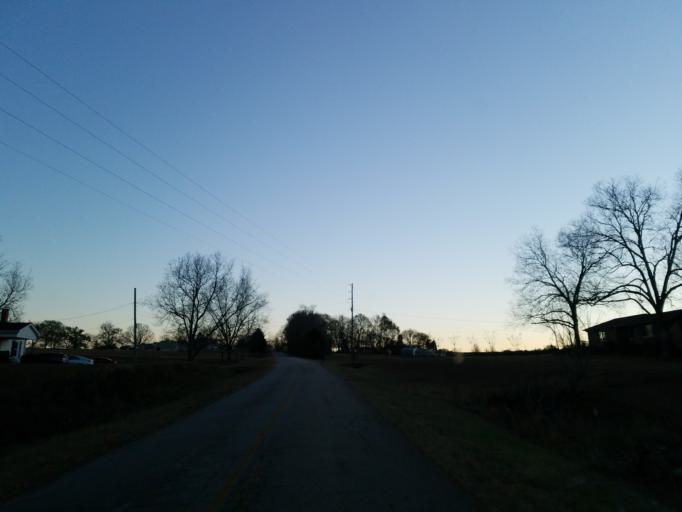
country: US
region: Georgia
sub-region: Monroe County
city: Forsyth
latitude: 32.9877
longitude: -83.8795
